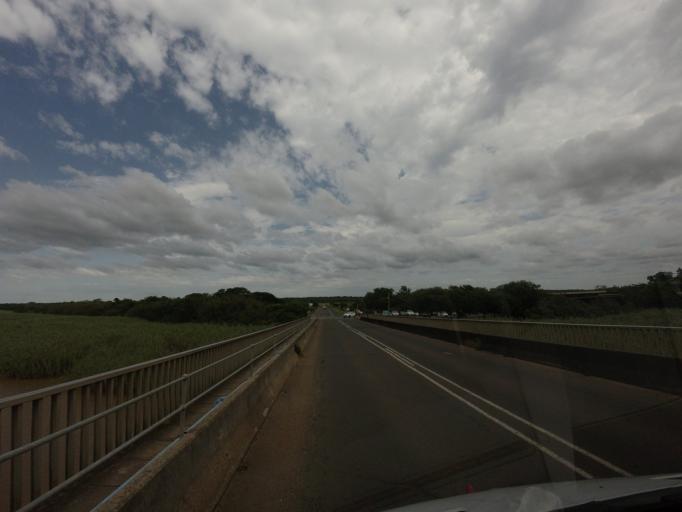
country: ZA
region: KwaZulu-Natal
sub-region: uMkhanyakude District Municipality
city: Mtubatuba
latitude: -28.3700
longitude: 32.4103
